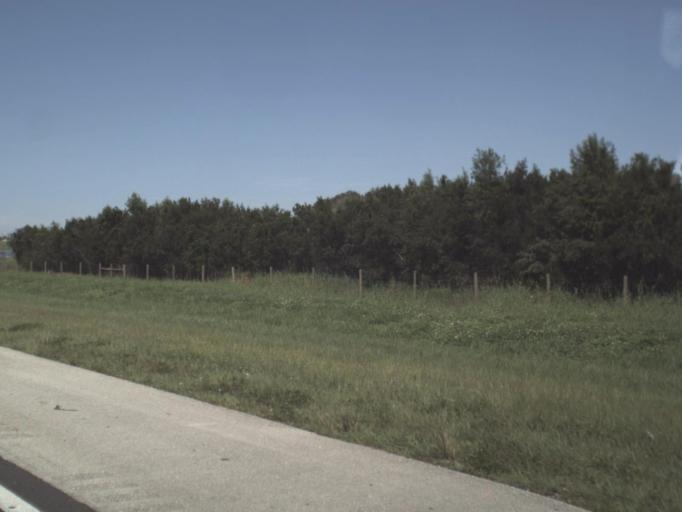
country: US
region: Florida
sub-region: Lee County
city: Bonita Springs
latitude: 26.3668
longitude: -81.7663
